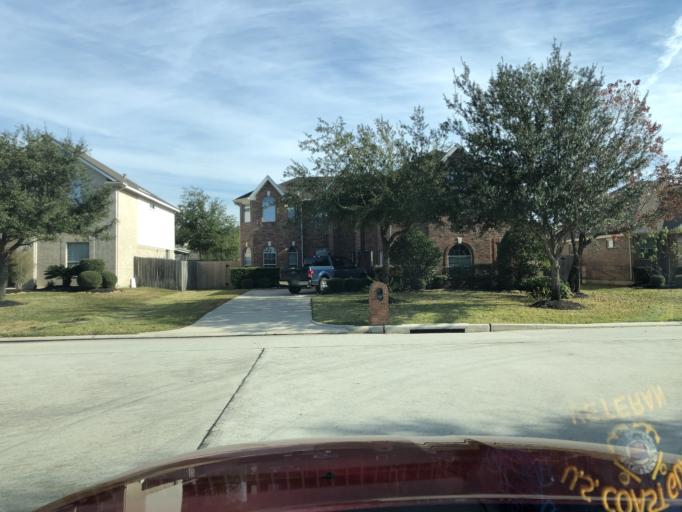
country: US
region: Texas
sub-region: Harris County
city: Tomball
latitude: 30.0248
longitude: -95.5620
